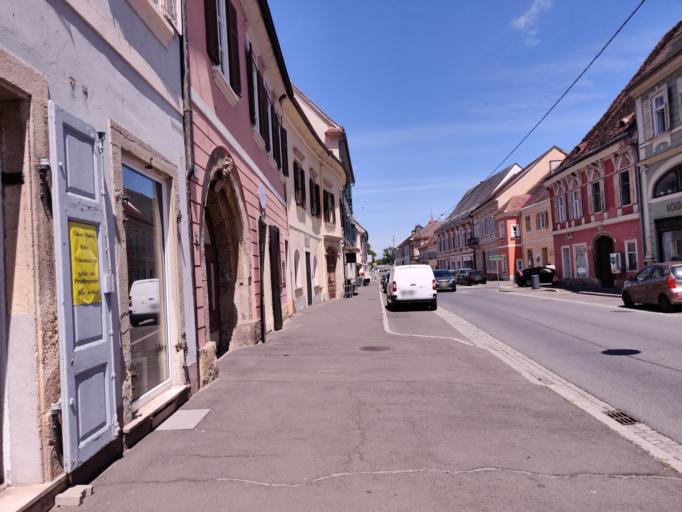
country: AT
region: Styria
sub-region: Politischer Bezirk Suedoststeiermark
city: Bad Radkersburg
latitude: 46.6885
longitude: 15.9864
